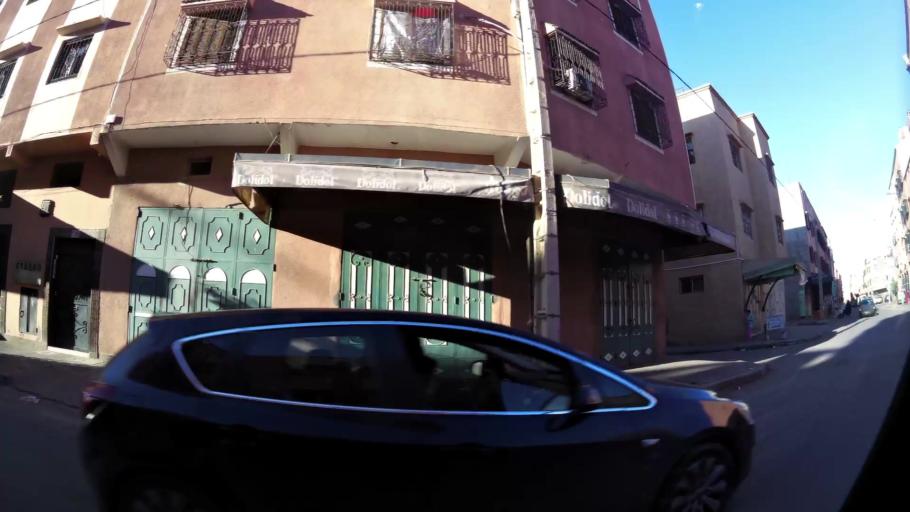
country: MA
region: Marrakech-Tensift-Al Haouz
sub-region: Marrakech
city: Marrakesh
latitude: 31.6197
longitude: -8.0620
